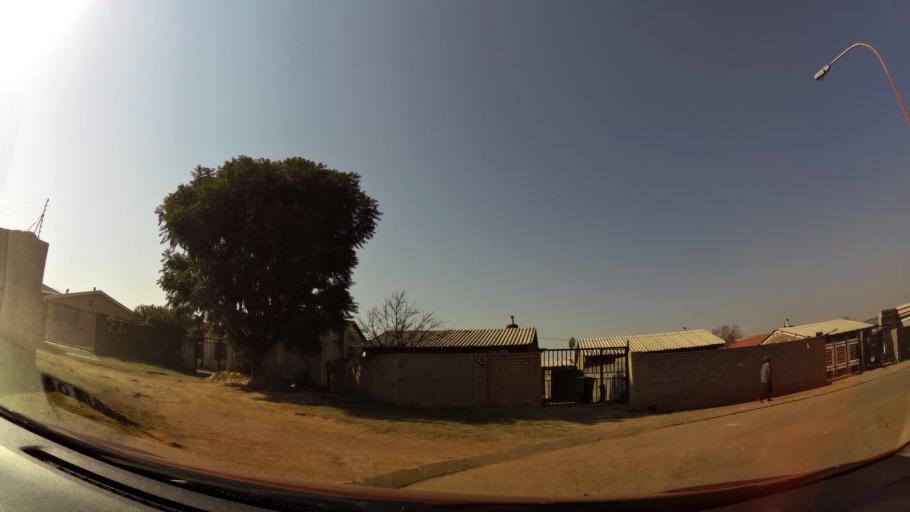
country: ZA
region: Gauteng
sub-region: City of Johannesburg Metropolitan Municipality
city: Soweto
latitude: -26.2451
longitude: 27.9479
